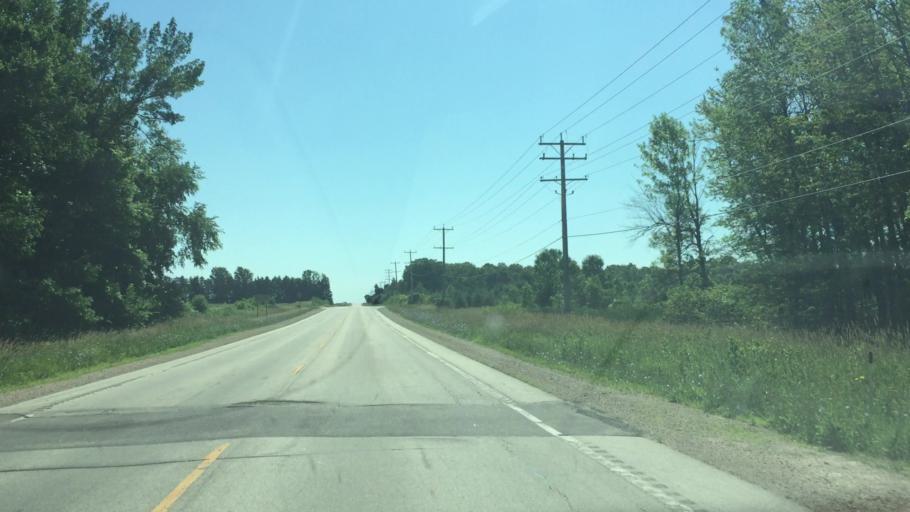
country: US
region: Wisconsin
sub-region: Calumet County
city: Sherwood
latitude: 44.1408
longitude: -88.2474
